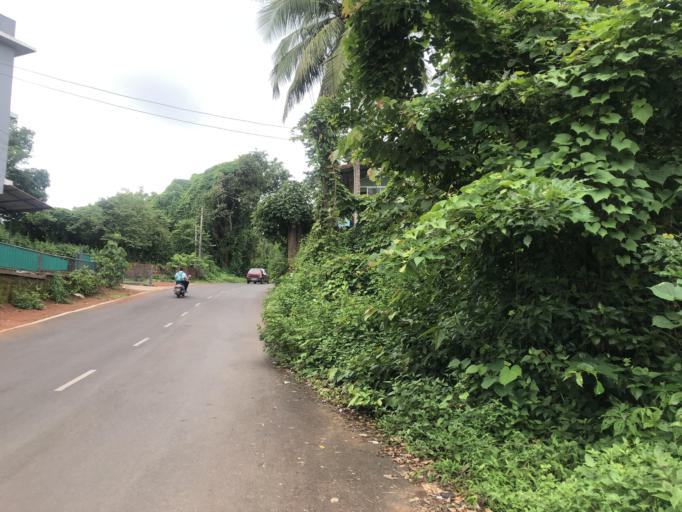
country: IN
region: Goa
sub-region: North Goa
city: Serula
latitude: 15.5404
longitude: 73.8317
